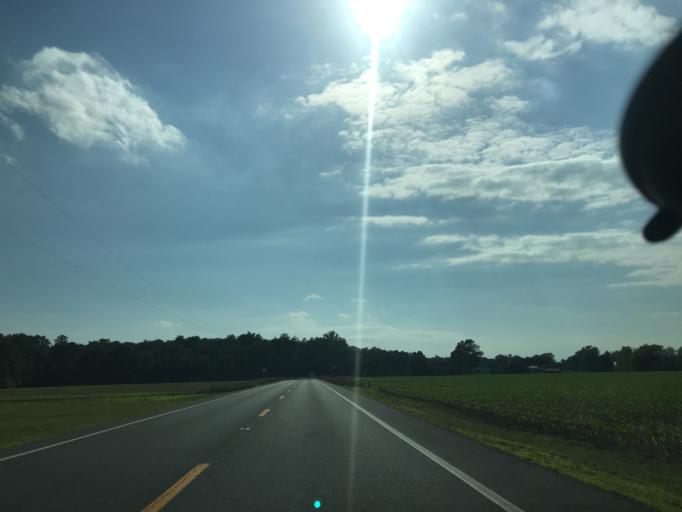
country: US
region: Maryland
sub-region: Wicomico County
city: Hebron
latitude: 38.4598
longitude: -75.6946
